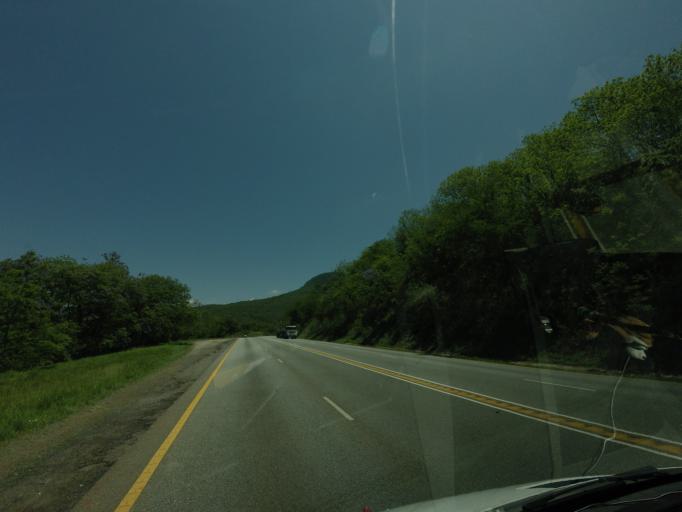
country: ZA
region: Mpumalanga
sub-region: Ehlanzeni District
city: Nelspruit
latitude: -25.4235
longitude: 30.7705
